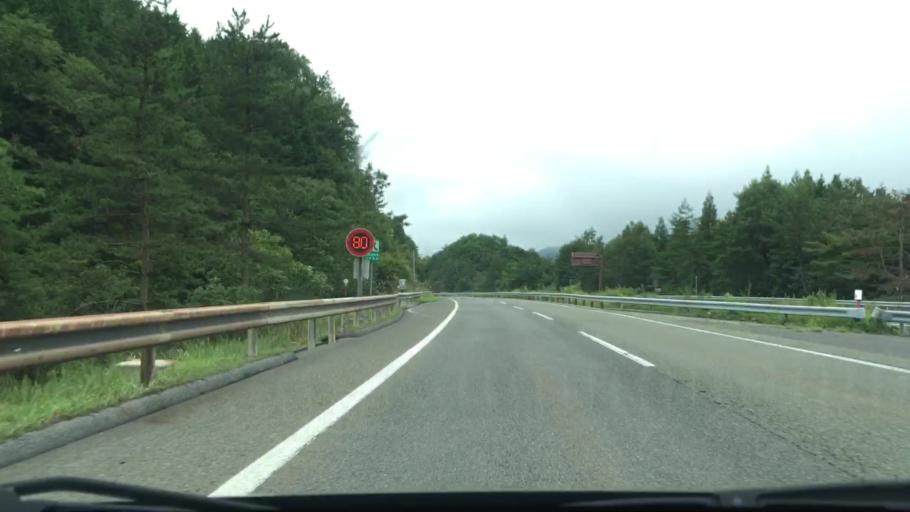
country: JP
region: Hiroshima
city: Shobara
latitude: 34.8751
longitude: 133.1217
